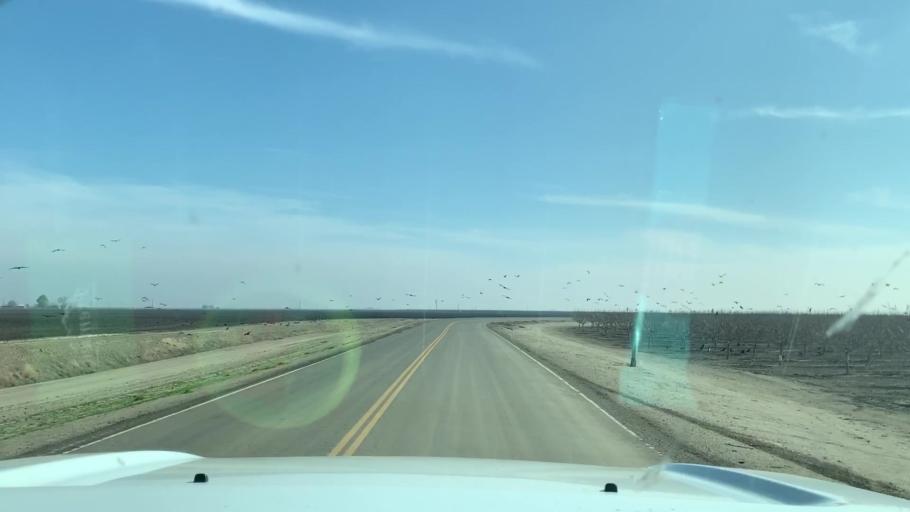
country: US
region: California
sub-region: Kern County
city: Buttonwillow
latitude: 35.4537
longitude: -119.5637
